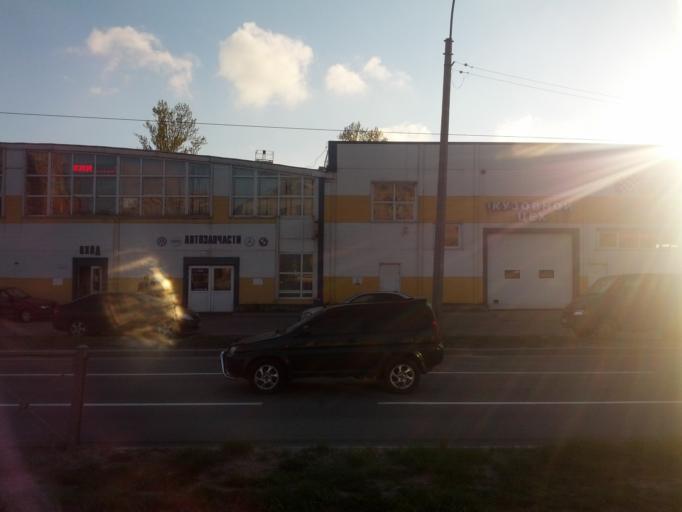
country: RU
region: St.-Petersburg
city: Obukhovo
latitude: 59.9020
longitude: 30.4581
